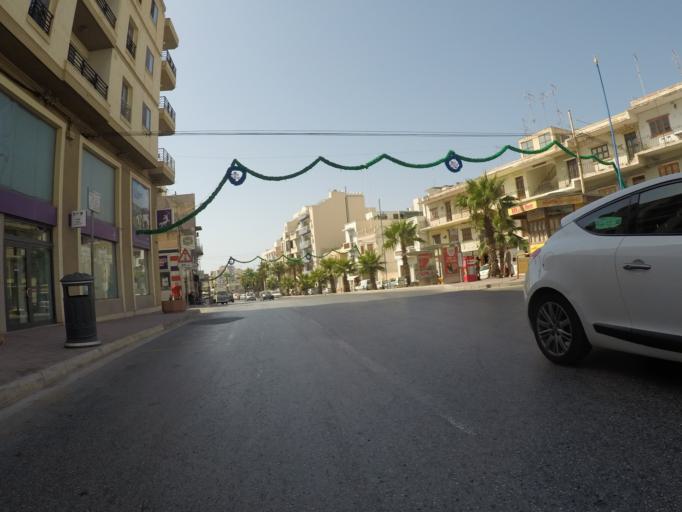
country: MT
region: Saint Paul's Bay
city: San Pawl il-Bahar
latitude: 35.9464
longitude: 14.4087
